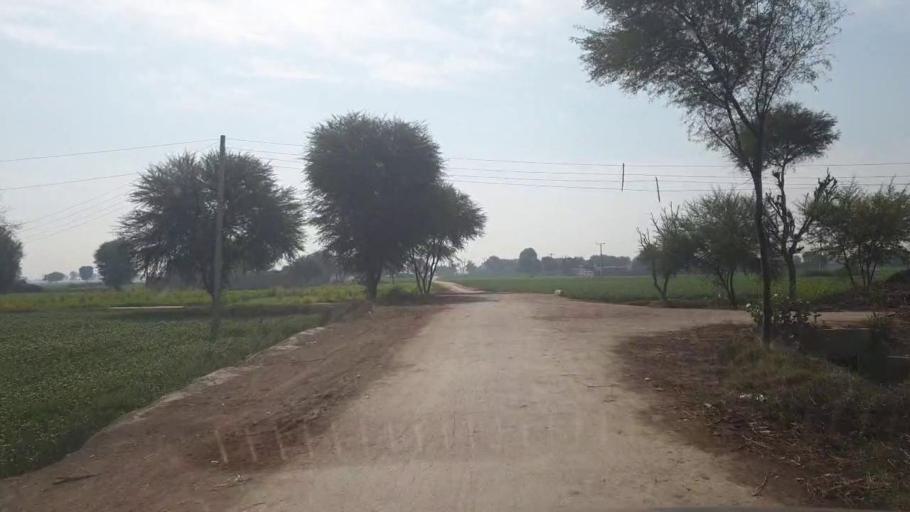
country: PK
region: Sindh
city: Nawabshah
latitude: 26.1608
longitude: 68.5020
